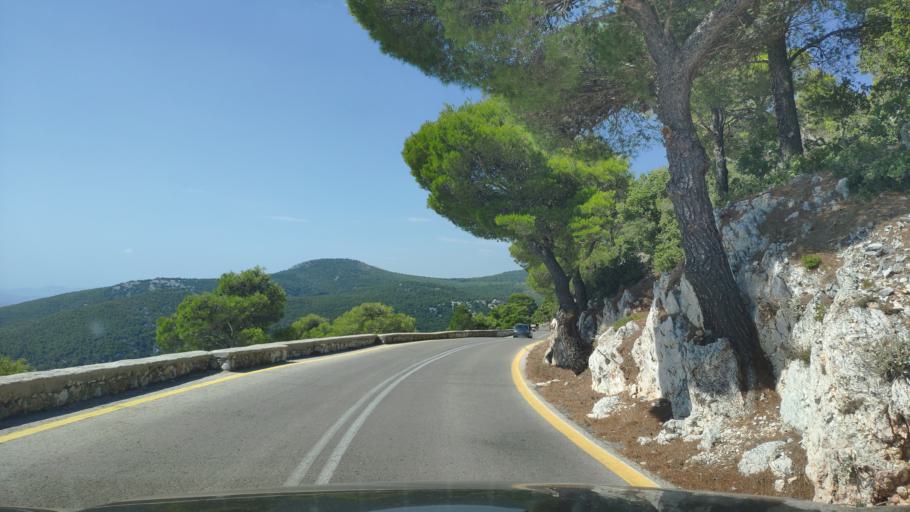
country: GR
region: Attica
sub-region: Nomarchia Anatolikis Attikis
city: Thrakomakedones
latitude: 38.1419
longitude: 23.7218
